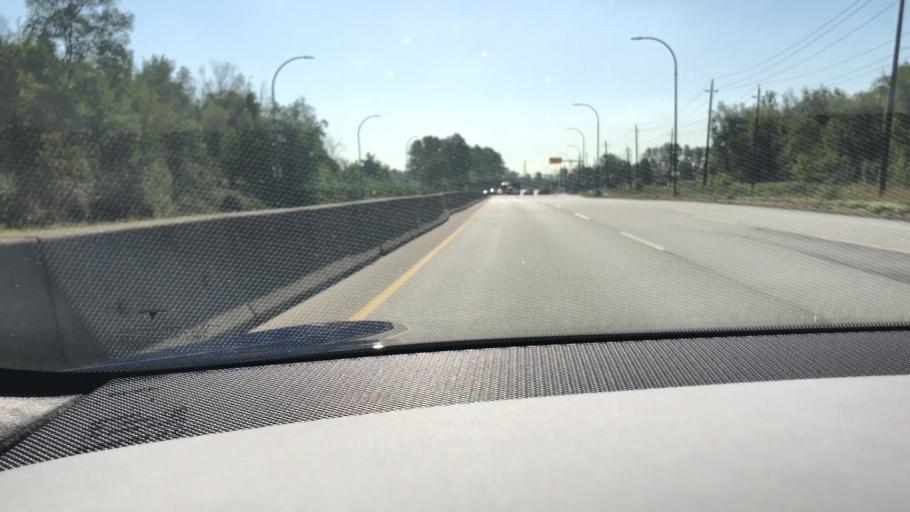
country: CA
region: British Columbia
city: New Westminster
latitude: 49.1972
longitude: -122.9725
